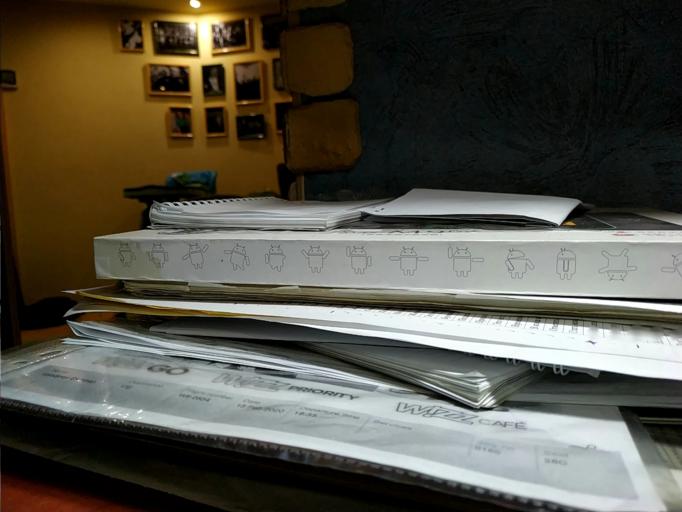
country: RU
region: Arkhangelskaya
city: Konevo
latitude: 61.9276
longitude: 39.0715
